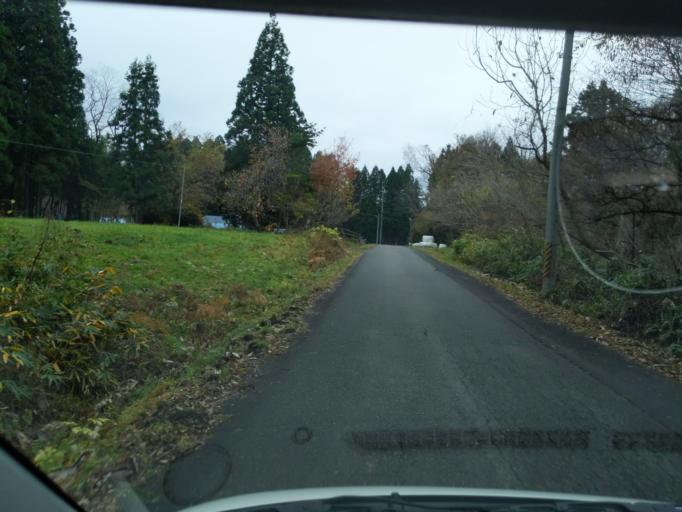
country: JP
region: Iwate
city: Ichinoseki
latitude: 38.9703
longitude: 140.9894
